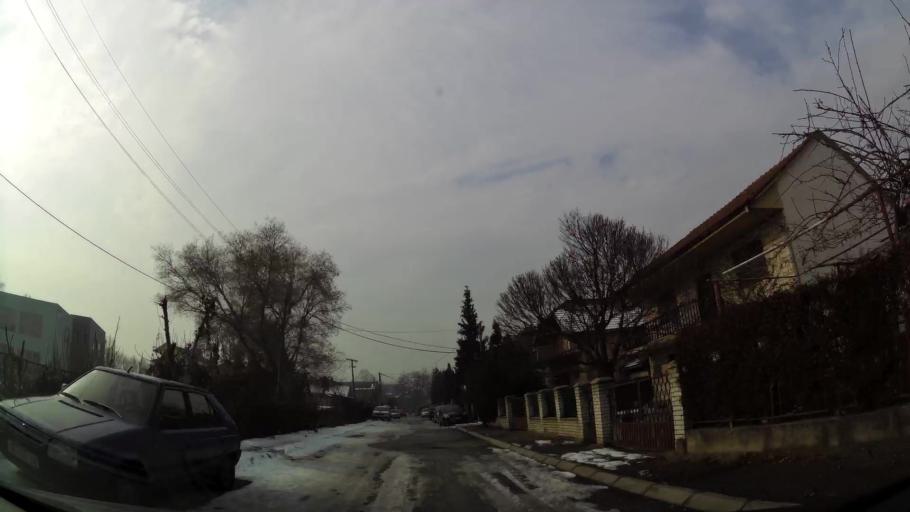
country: MK
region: Kisela Voda
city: Kisela Voda
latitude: 41.9958
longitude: 21.5076
